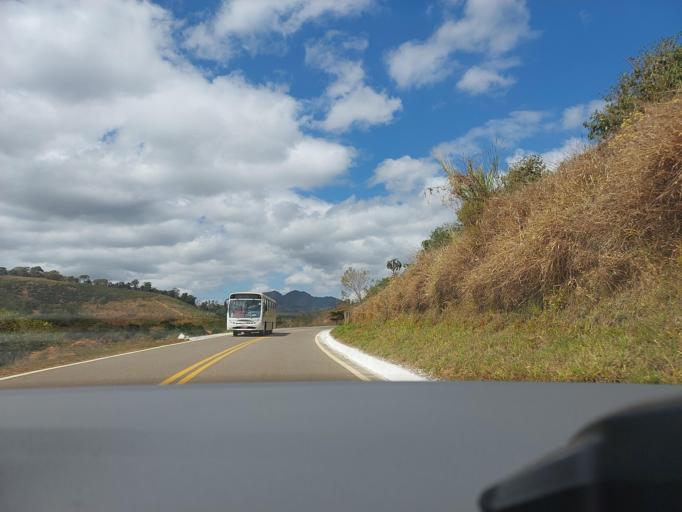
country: BR
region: Minas Gerais
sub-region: Visconde Do Rio Branco
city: Visconde do Rio Branco
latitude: -20.9310
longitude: -42.6335
